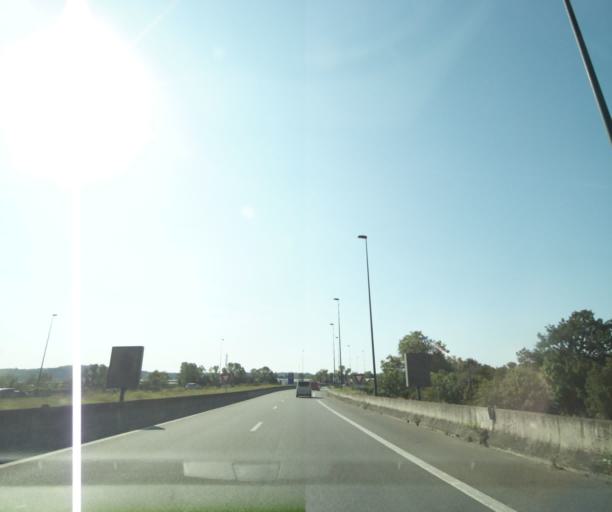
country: FR
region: Midi-Pyrenees
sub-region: Departement de la Haute-Garonne
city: Portet-sur-Garonne
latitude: 43.5669
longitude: 1.4171
